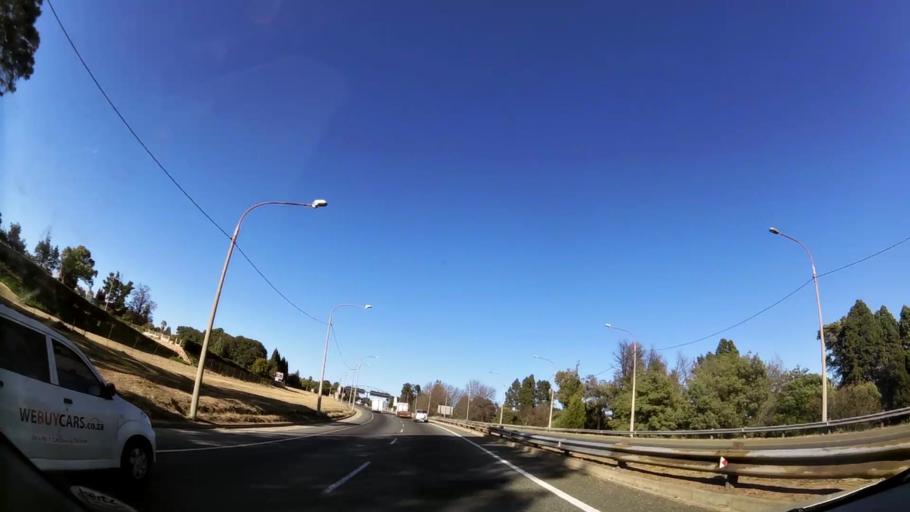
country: ZA
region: Gauteng
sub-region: West Rand District Municipality
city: Krugersdorp
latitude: -26.0800
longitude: 27.7900
